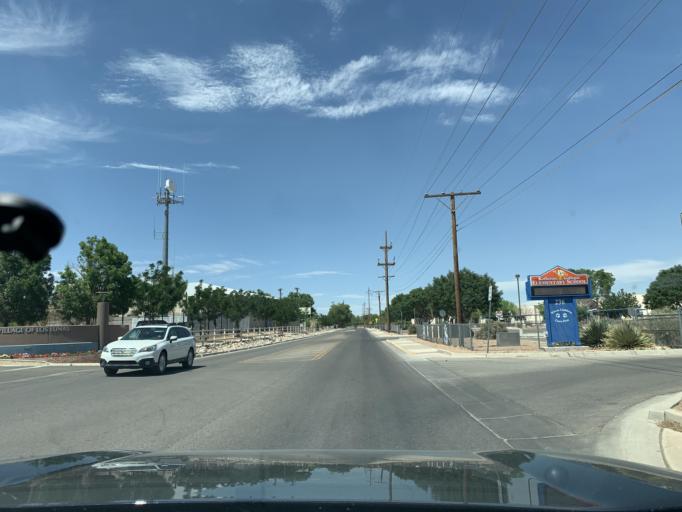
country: US
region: New Mexico
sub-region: Valencia County
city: Los Lunas
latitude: 34.8114
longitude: -106.7406
